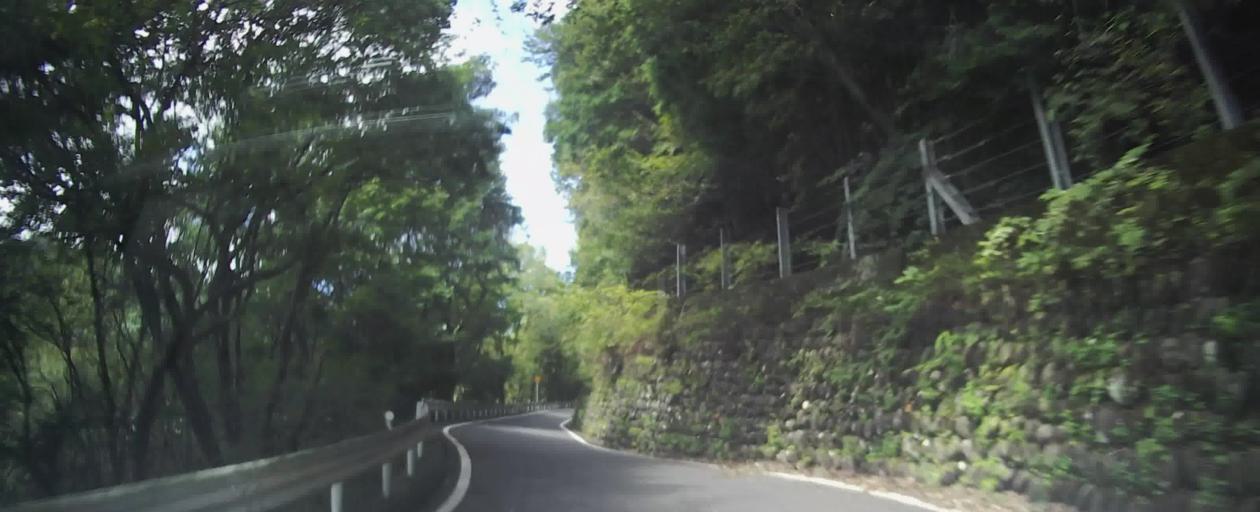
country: JP
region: Gunma
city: Kanekomachi
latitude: 36.4463
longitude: 138.9058
